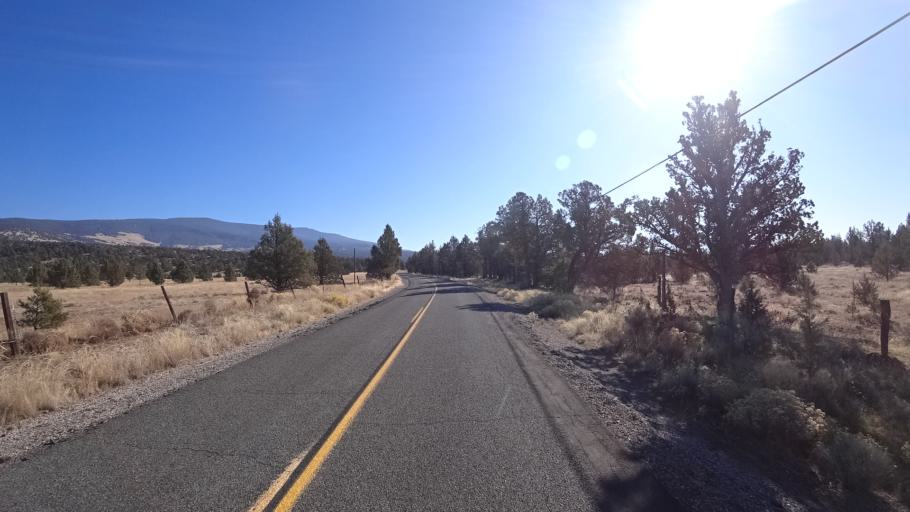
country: US
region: California
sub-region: Siskiyou County
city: Montague
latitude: 41.6414
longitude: -122.3461
